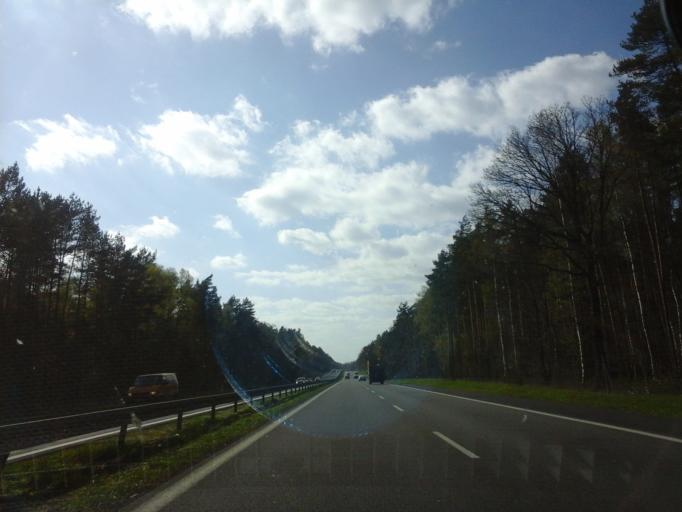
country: PL
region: West Pomeranian Voivodeship
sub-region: Powiat gryfinski
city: Stare Czarnowo
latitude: 53.3581
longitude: 14.7798
